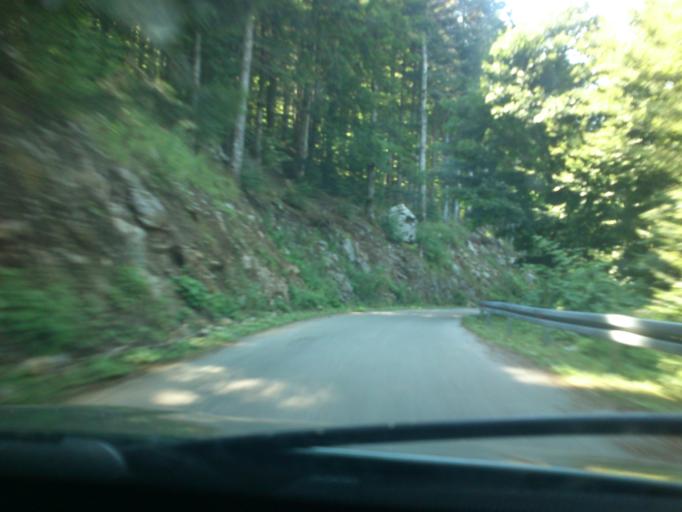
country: HR
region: Licko-Senjska
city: Senj
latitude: 44.8466
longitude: 14.9908
